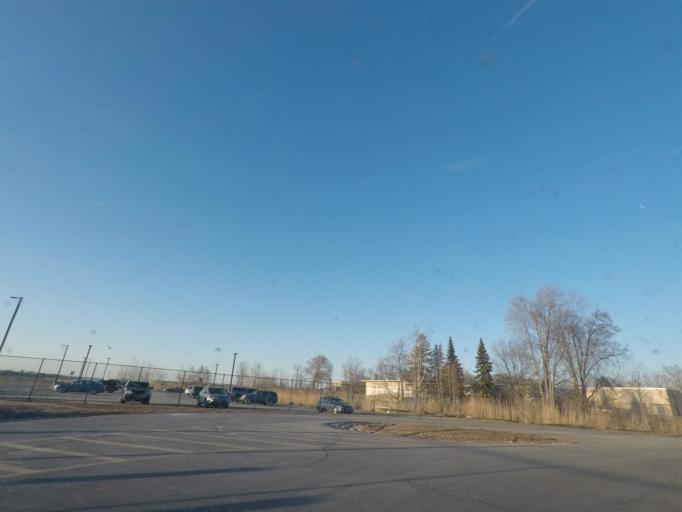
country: US
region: New York
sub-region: Albany County
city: Colonie
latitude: 42.7393
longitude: -73.8015
